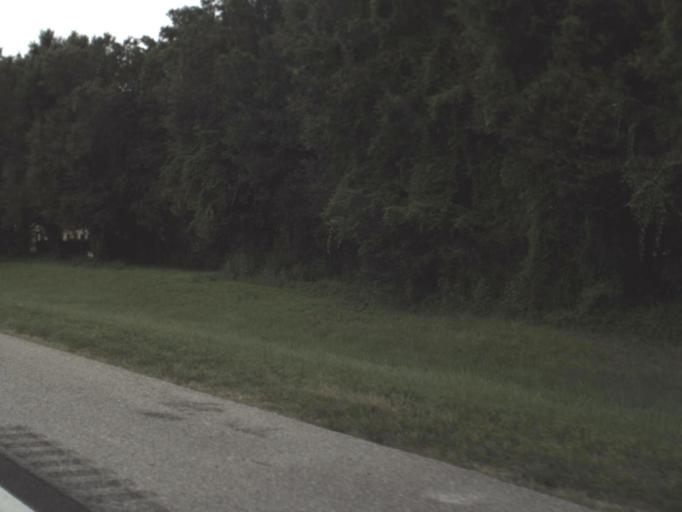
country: US
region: Florida
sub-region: Sarasota County
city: Fruitville
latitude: 27.3148
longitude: -82.4482
